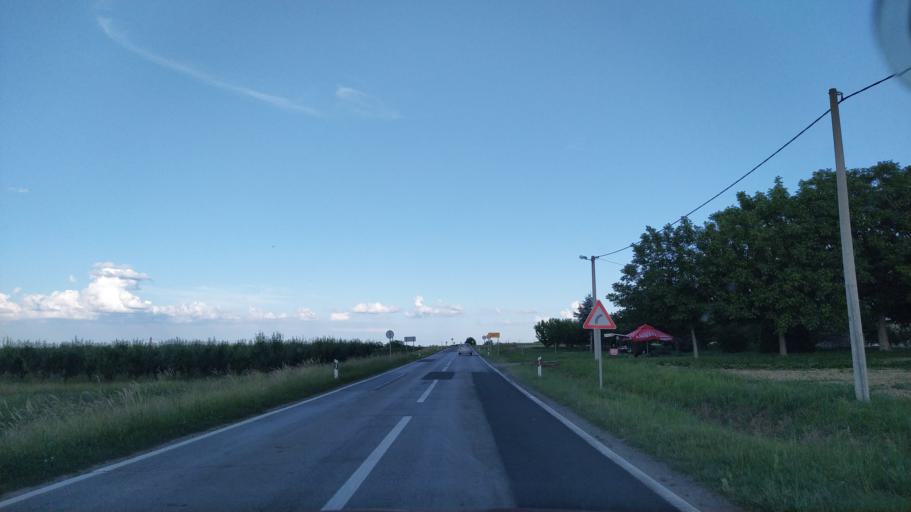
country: HR
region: Virovitick-Podravska
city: Suhopolje
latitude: 45.7479
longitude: 17.5944
